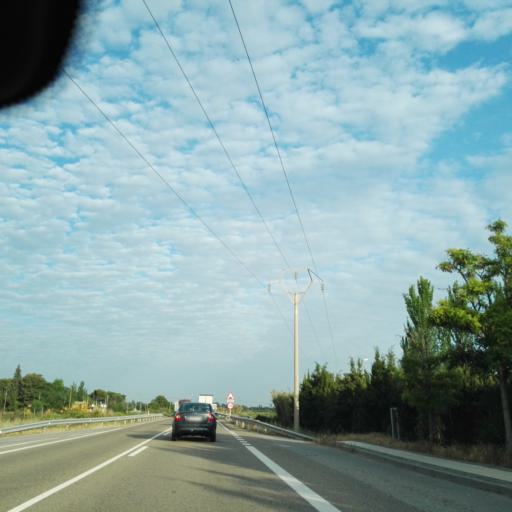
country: ES
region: Aragon
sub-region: Provincia de Zaragoza
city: Utebo
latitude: 41.6638
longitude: -0.9923
